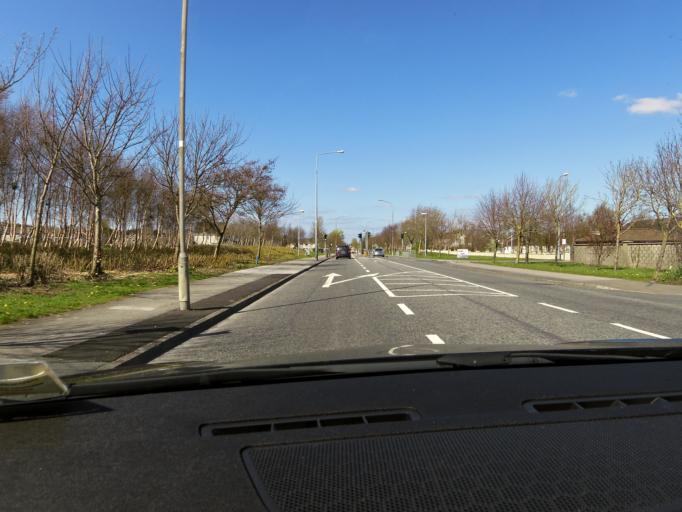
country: IE
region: Connaught
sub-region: County Galway
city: Gaillimh
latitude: 53.2824
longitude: -9.0720
